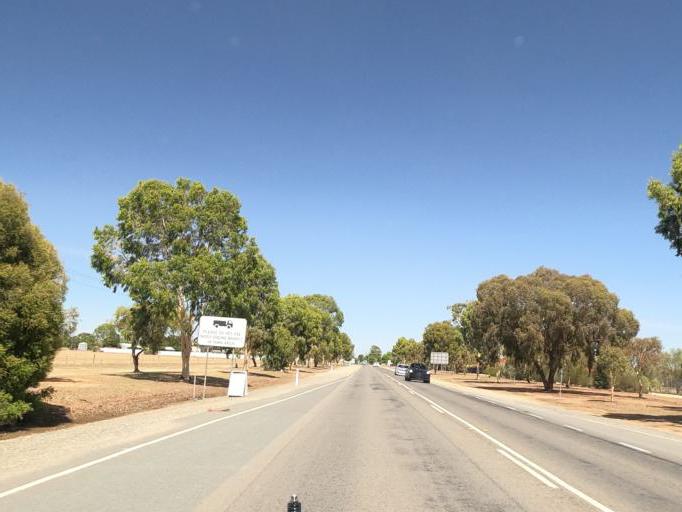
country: AU
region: Victoria
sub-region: Moira
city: Yarrawonga
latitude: -36.0137
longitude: 146.0174
